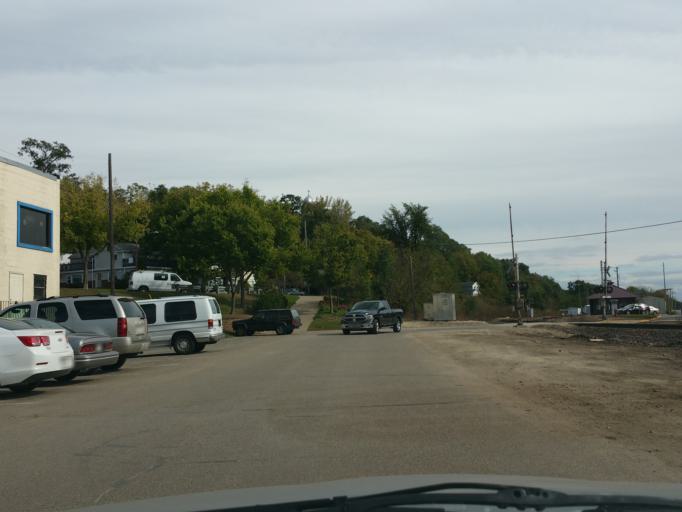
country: US
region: Wisconsin
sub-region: Pierce County
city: Prescott
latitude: 44.7479
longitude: -92.8015
